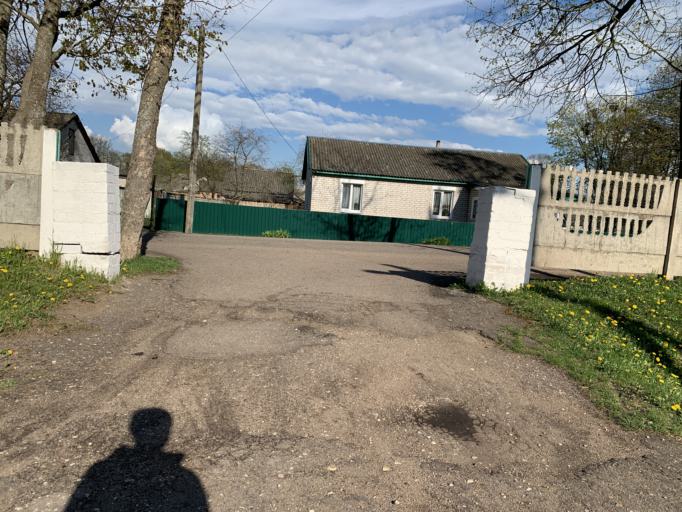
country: BY
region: Minsk
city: Kapyl'
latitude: 53.2596
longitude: 26.9524
